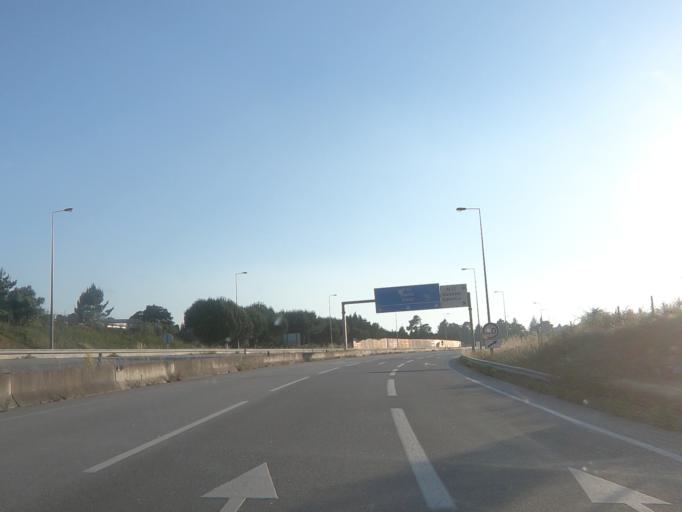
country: PT
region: Guarda
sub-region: Celorico da Beira
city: Celorico da Beira
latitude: 40.6242
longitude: -7.3972
